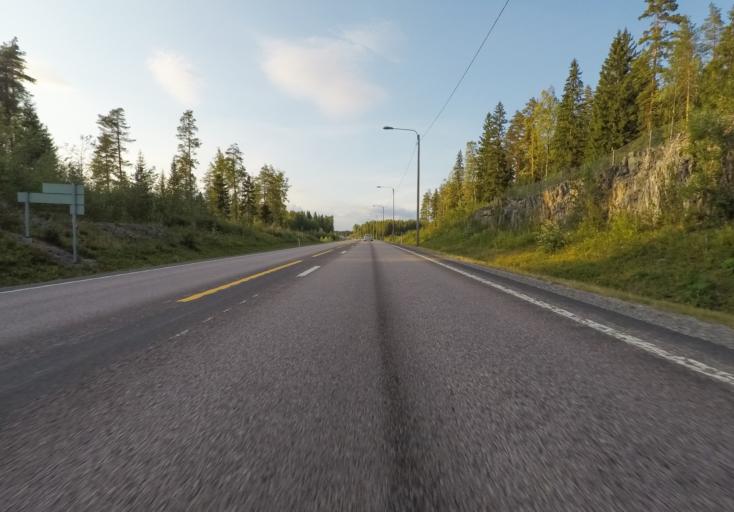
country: FI
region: Paijanne Tavastia
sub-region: Lahti
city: Heinola
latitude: 61.3494
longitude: 26.0442
